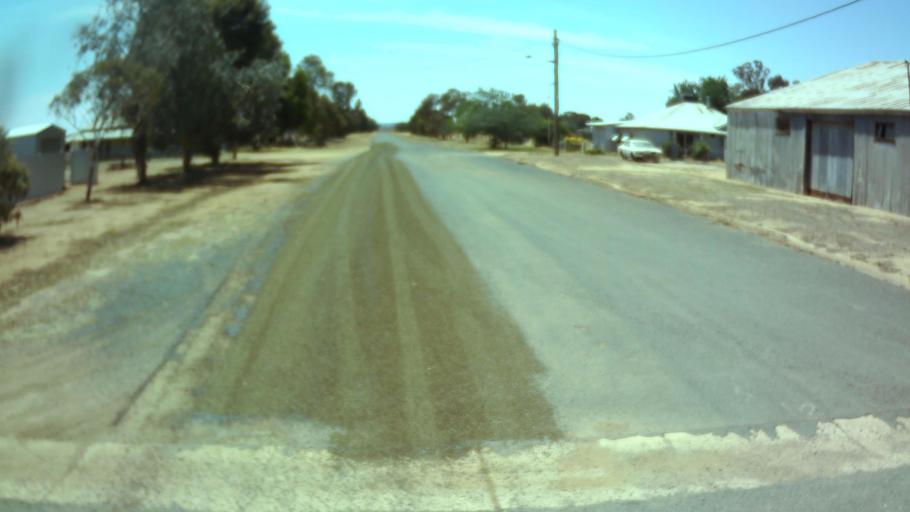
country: AU
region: New South Wales
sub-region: Weddin
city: Grenfell
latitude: -33.8435
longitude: 147.7391
